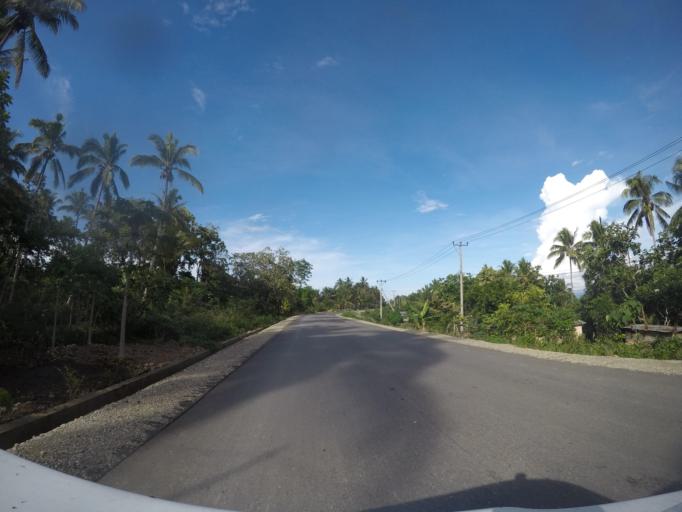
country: TL
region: Baucau
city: Baucau
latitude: -8.5030
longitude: 126.4470
